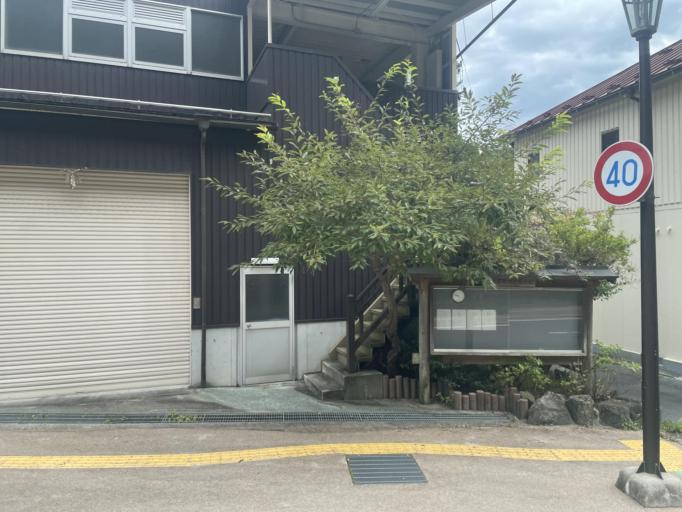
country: JP
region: Wakayama
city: Koya
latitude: 34.2159
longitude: 135.5836
